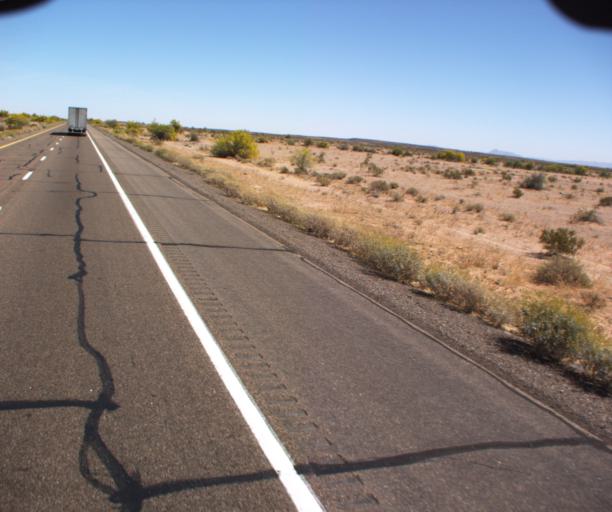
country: US
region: Arizona
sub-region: Maricopa County
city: Gila Bend
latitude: 32.8665
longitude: -113.1532
